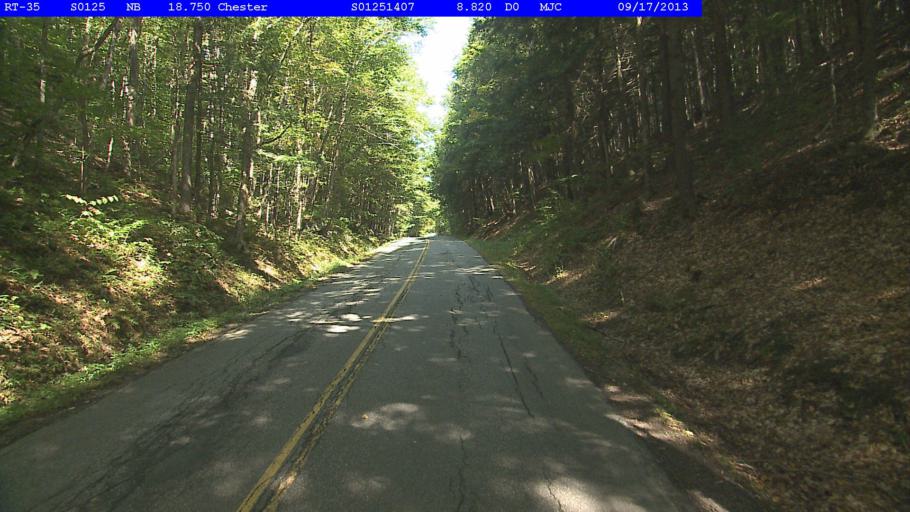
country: US
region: Vermont
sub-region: Windsor County
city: Chester
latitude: 43.2327
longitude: -72.6071
